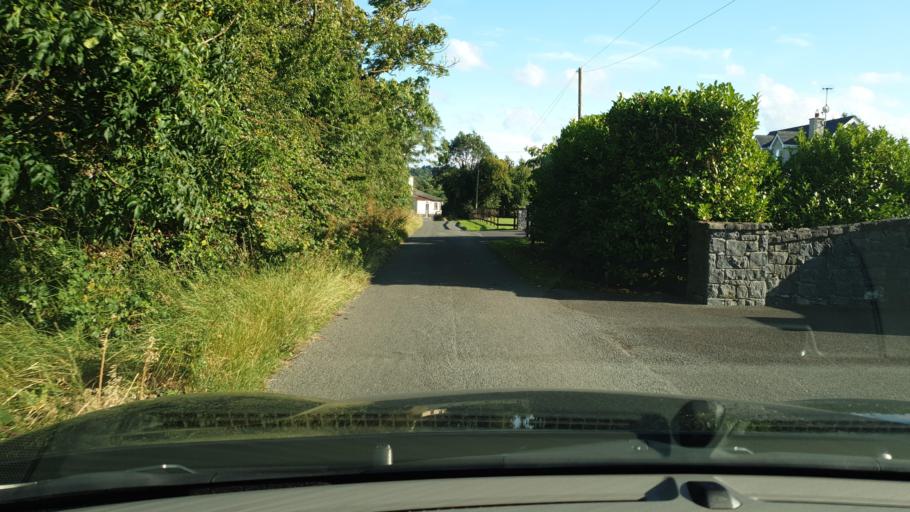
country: IE
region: Leinster
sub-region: An Mhi
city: Stamullin
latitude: 53.5882
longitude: -6.2524
